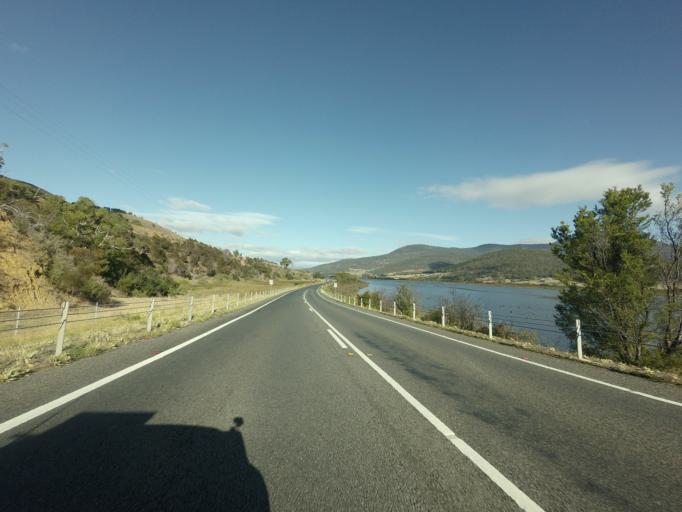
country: AU
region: Tasmania
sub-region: Brighton
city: Bridgewater
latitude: -42.7446
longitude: 147.1854
